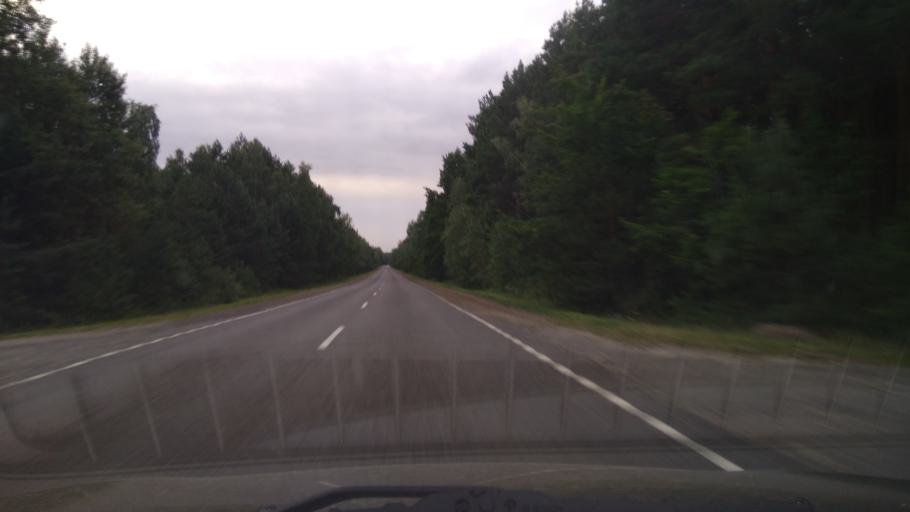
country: BY
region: Brest
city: Byaroza
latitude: 52.4062
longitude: 24.9988
